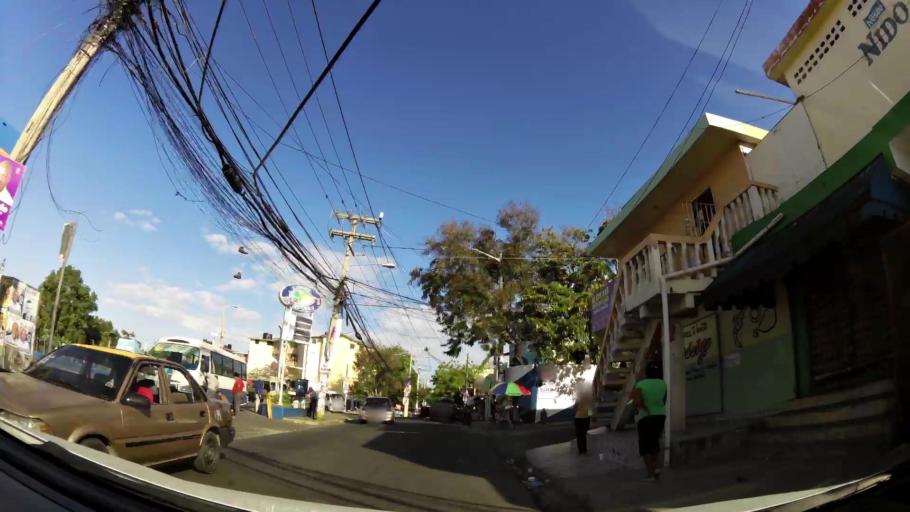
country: DO
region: Santo Domingo
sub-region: Santo Domingo
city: Santo Domingo Este
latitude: 18.4729
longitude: -69.8515
